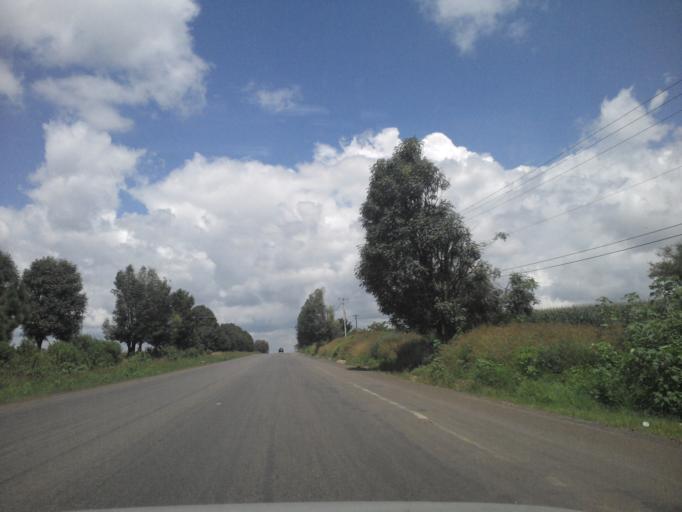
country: MX
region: Jalisco
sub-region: Atotonilco el Alto
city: Ojo de Agua de Moran
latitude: 20.5848
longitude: -102.4974
